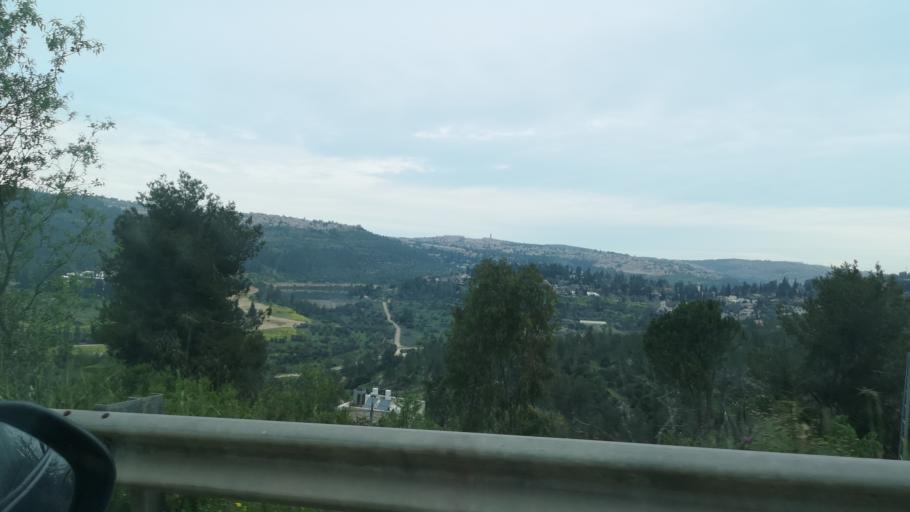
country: PS
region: West Bank
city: Bayt Iksa
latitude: 31.7703
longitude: 35.1601
